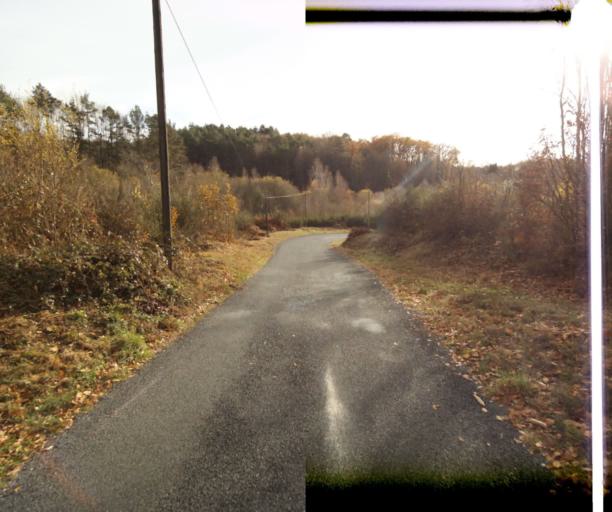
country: FR
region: Limousin
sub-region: Departement de la Correze
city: Sainte-Fortunade
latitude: 45.1887
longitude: 1.7899
